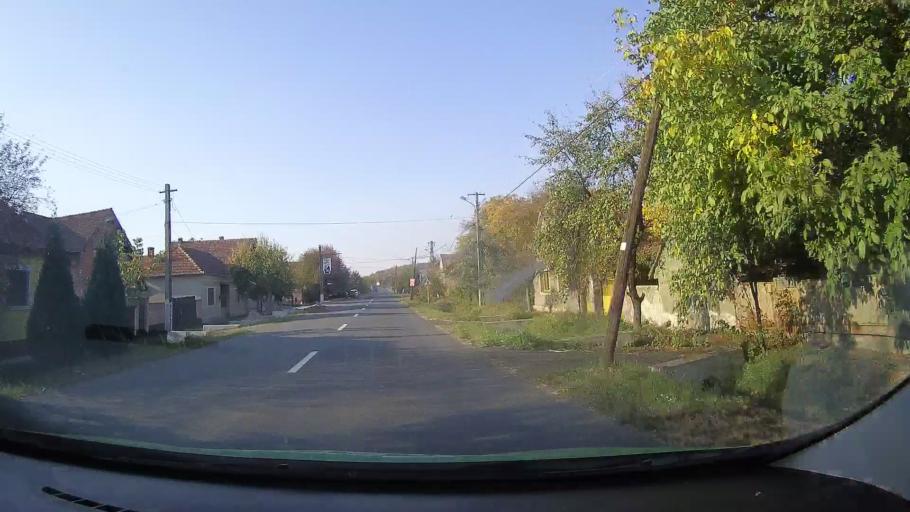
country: RO
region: Arad
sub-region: Comuna Ghioroc
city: Ghioroc
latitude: 46.1405
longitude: 21.6029
